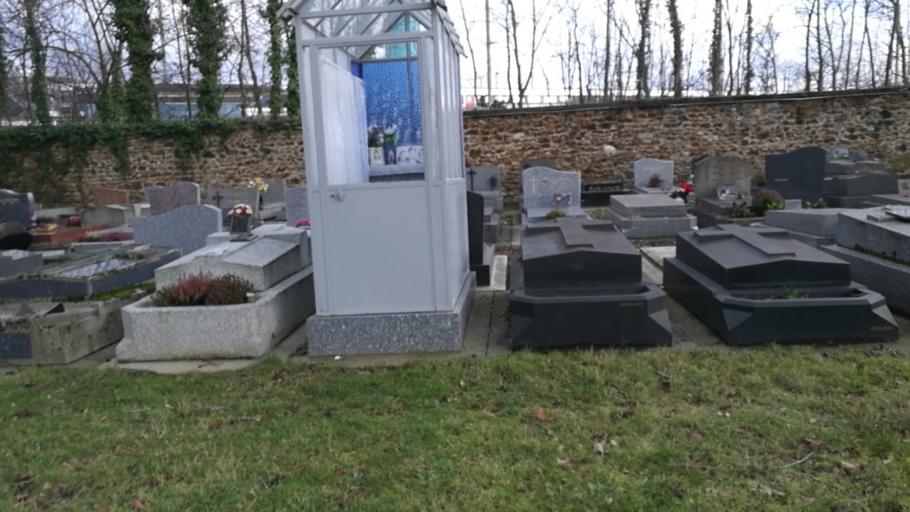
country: FR
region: Ile-de-France
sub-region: Paris
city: Saint-Ouen
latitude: 48.9068
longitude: 2.3505
